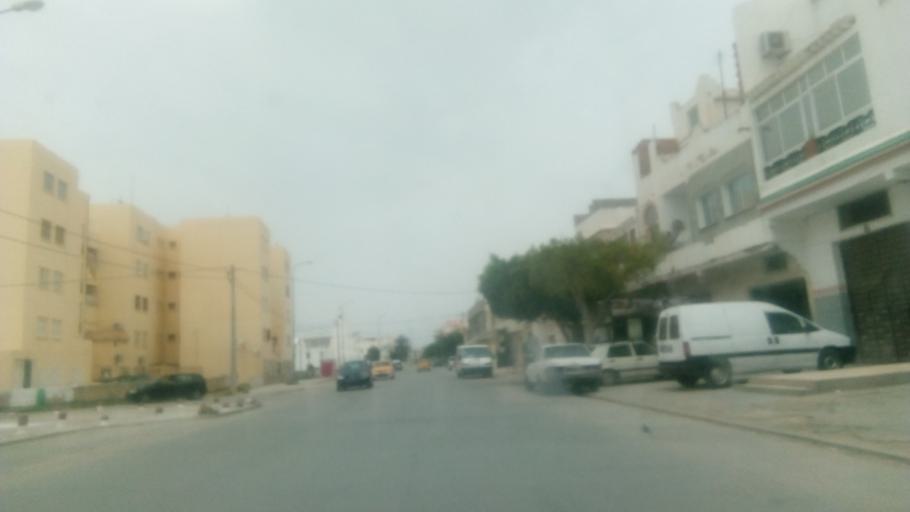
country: TN
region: Al Qayrawan
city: Kairouan
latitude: 35.6702
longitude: 10.0885
